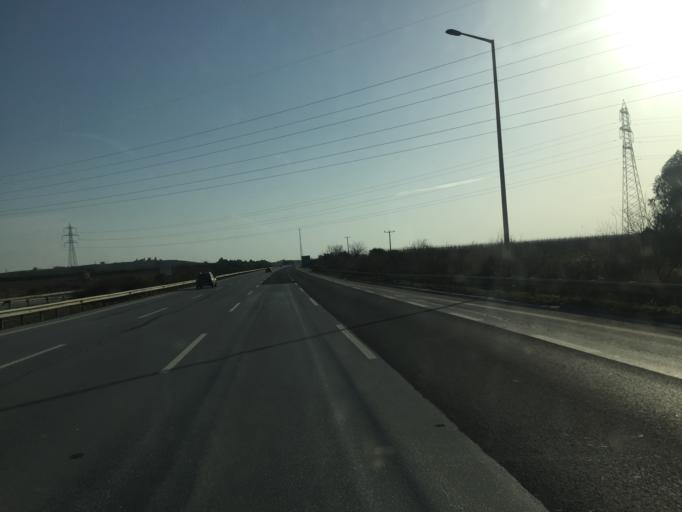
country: TR
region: Mersin
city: Yenice
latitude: 37.0234
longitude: 35.0696
